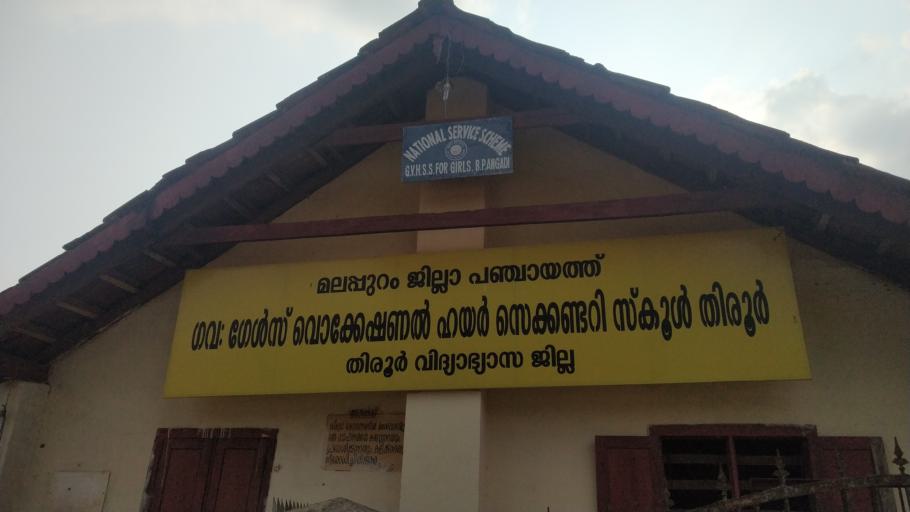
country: IN
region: Kerala
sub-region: Malappuram
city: Tirur
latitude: 10.8847
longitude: 75.9292
